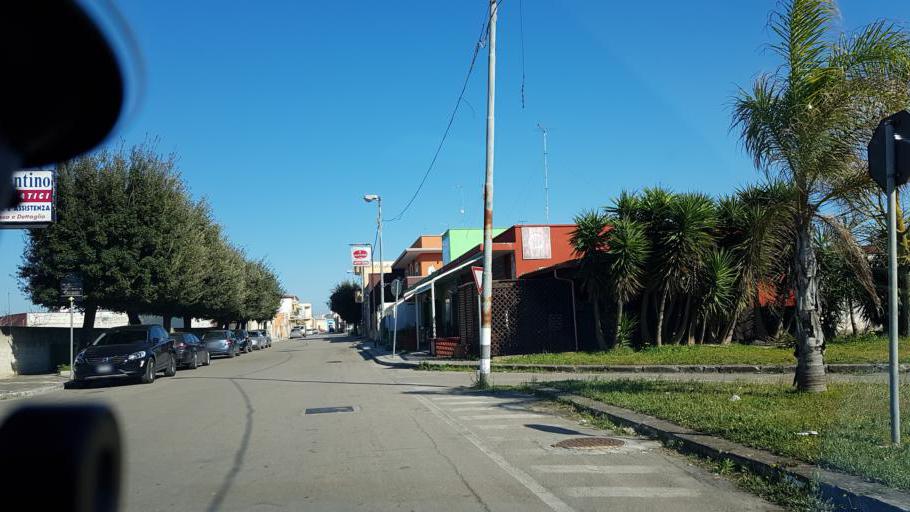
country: IT
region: Apulia
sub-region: Provincia di Brindisi
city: Torchiarolo
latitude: 40.4865
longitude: 18.0473
